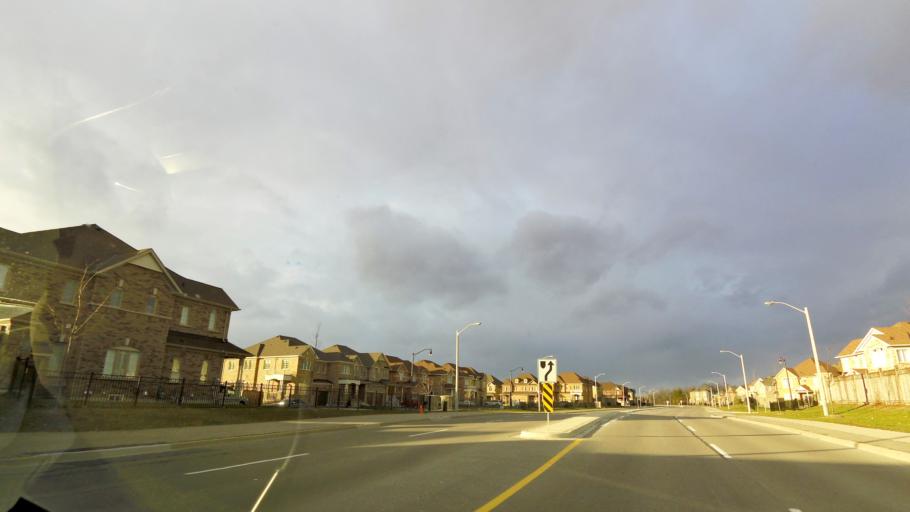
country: CA
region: Ontario
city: Brampton
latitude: 43.7862
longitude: -79.6638
